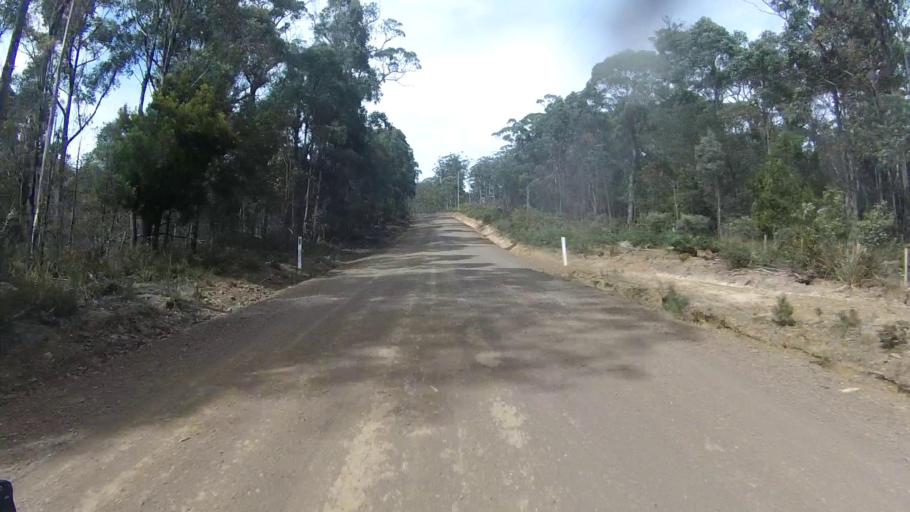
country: AU
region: Tasmania
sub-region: Sorell
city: Sorell
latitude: -42.6814
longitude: 147.8814
